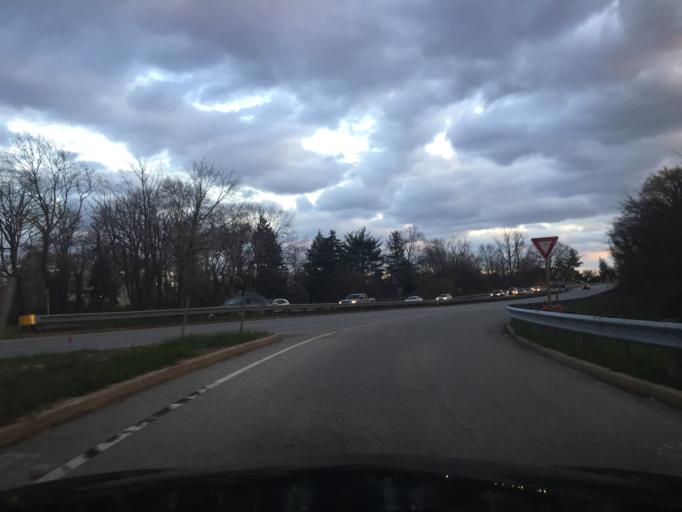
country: US
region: Maryland
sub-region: Baltimore County
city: Parkville
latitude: 39.3802
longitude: -76.5565
